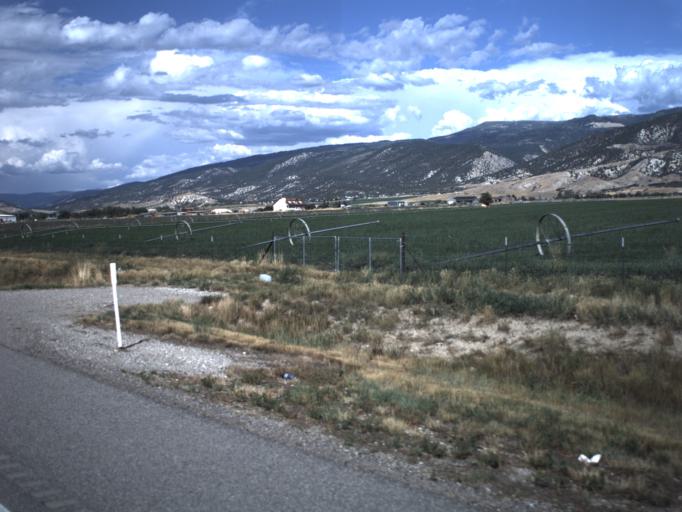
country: US
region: Utah
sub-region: Sanpete County
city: Ephraim
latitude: 39.3262
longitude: -111.6027
